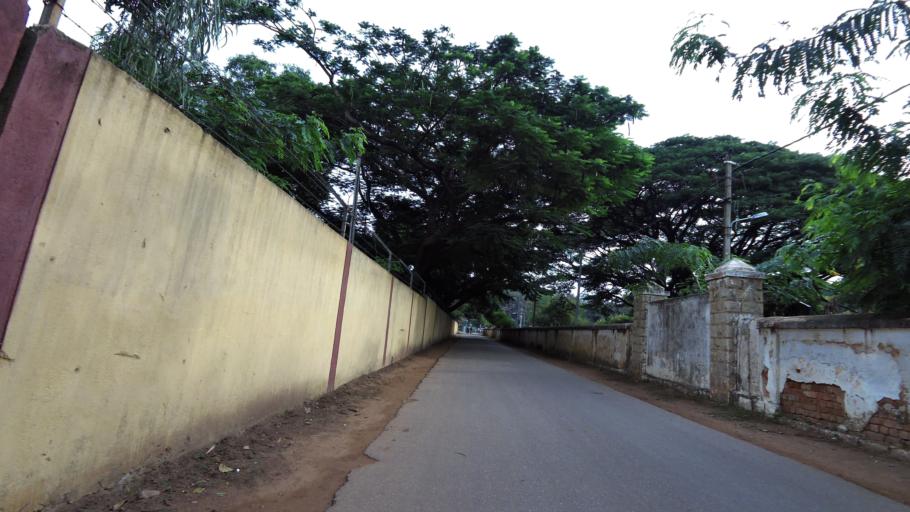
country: IN
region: Karnataka
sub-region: Bangalore Urban
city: Bangalore
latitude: 12.9927
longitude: 77.6316
